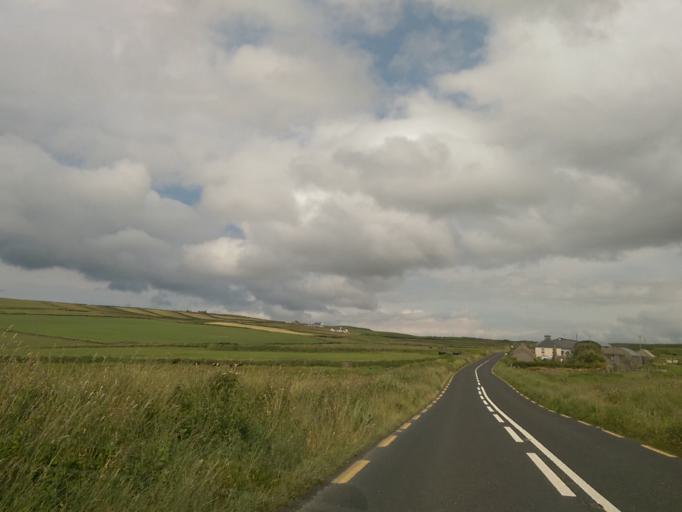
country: IE
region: Munster
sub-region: An Clar
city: Kilrush
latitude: 52.6918
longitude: -9.6376
